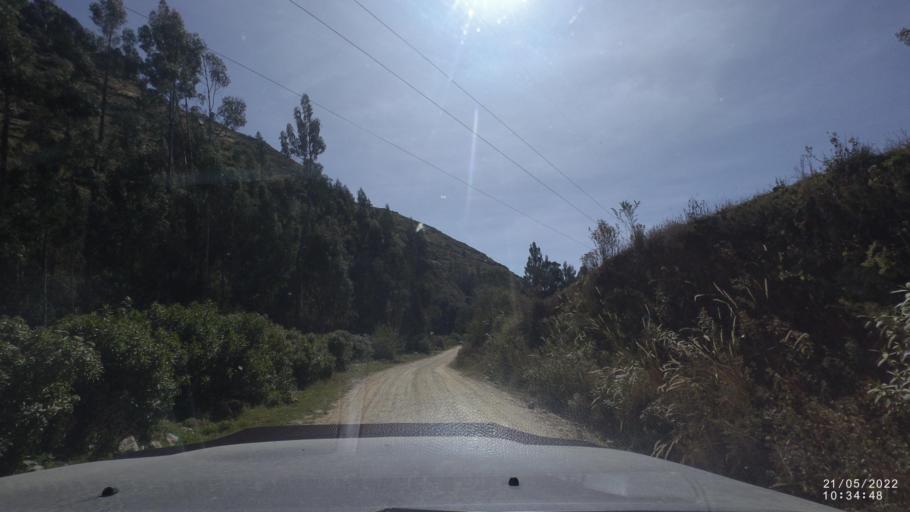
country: BO
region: Cochabamba
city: Colomi
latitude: -17.3196
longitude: -65.9302
